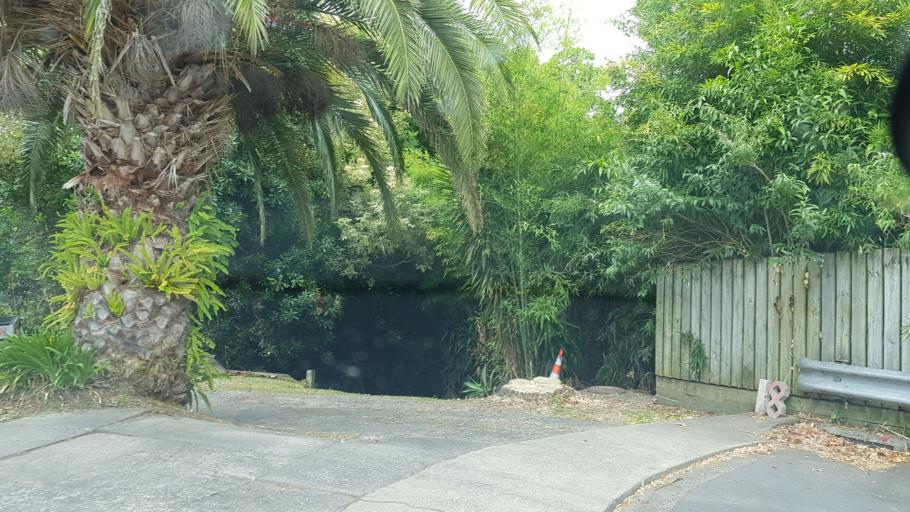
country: NZ
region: Auckland
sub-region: Auckland
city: North Shore
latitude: -36.8073
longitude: 174.7831
